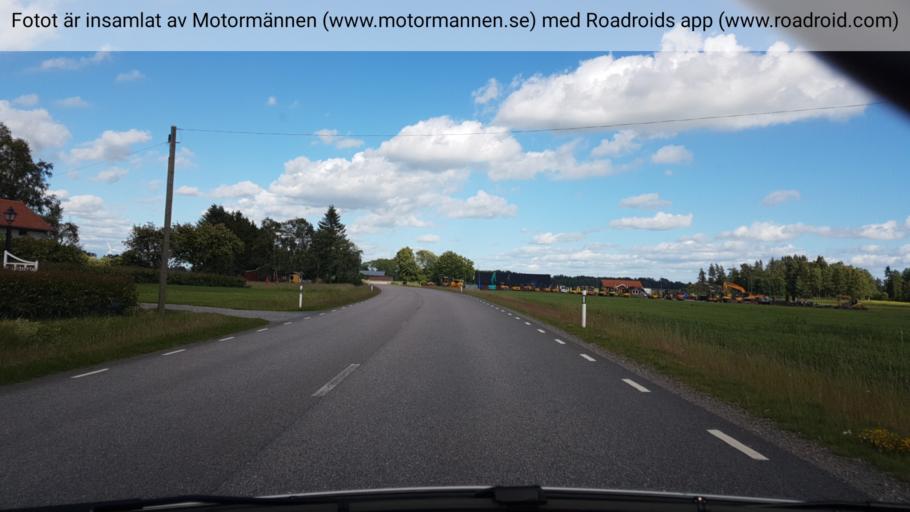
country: SE
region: Vaestra Goetaland
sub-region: Grastorps Kommun
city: Graestorp
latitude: 58.3266
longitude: 12.7227
